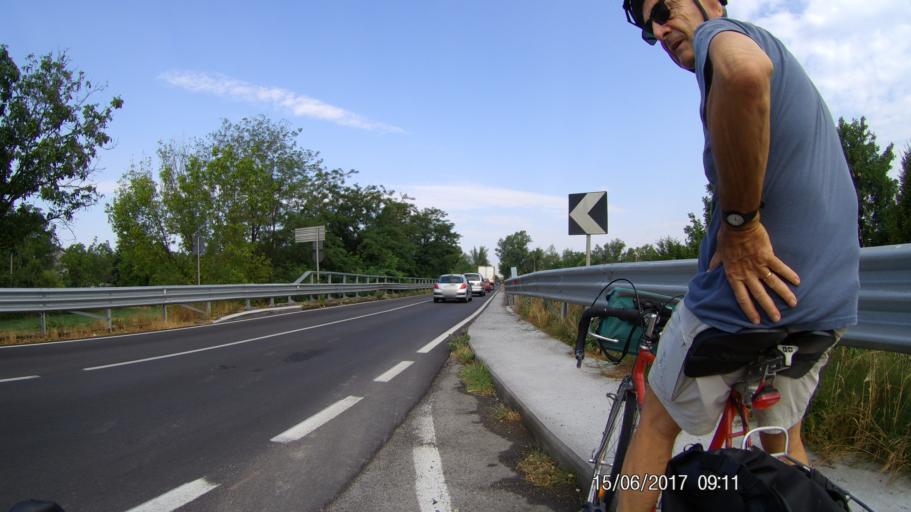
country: IT
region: Emilia-Romagna
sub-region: Provincia di Reggio Emilia
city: Sant'Ilario d'Enza
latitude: 44.7699
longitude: 10.4309
